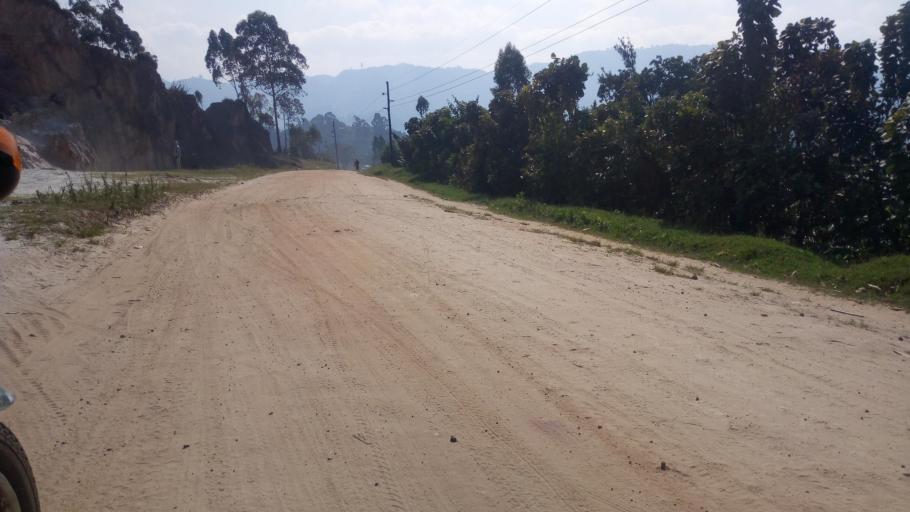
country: UG
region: Western Region
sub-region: Kisoro District
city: Kisoro
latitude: -1.2285
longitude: 29.7115
